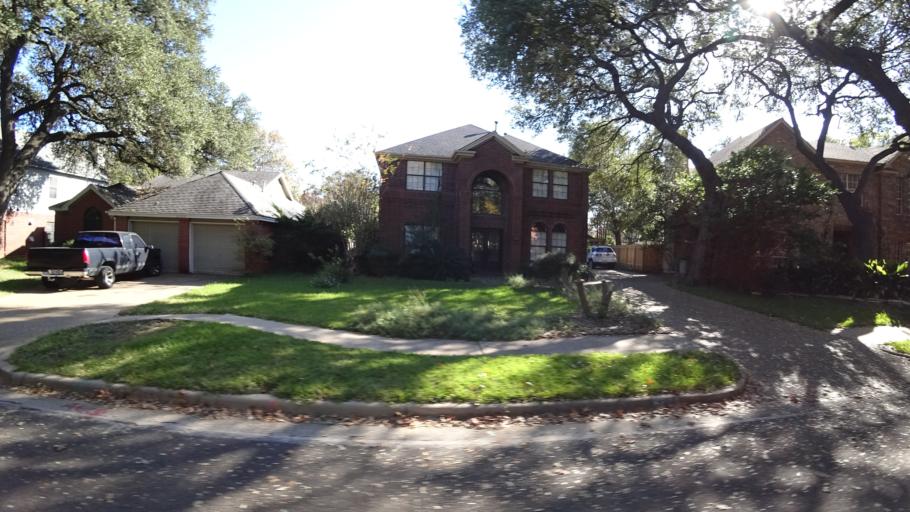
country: US
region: Texas
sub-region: Travis County
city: Shady Hollow
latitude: 30.2228
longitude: -97.8701
